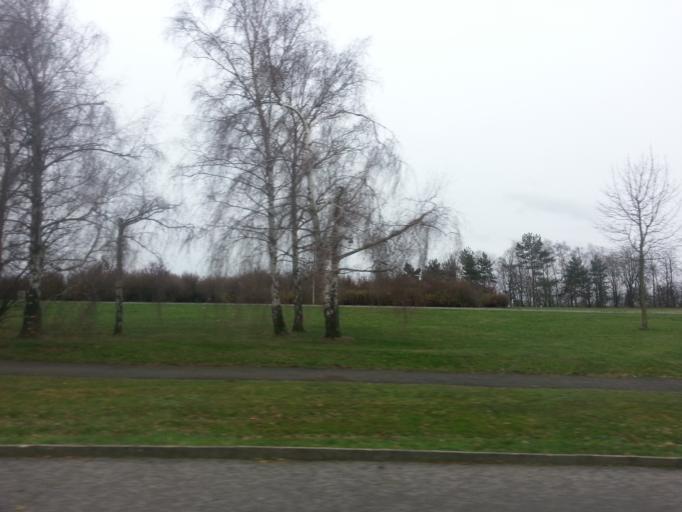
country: CZ
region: Praha
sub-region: Praha 1
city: Mala Strana
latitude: 50.0797
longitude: 14.3543
